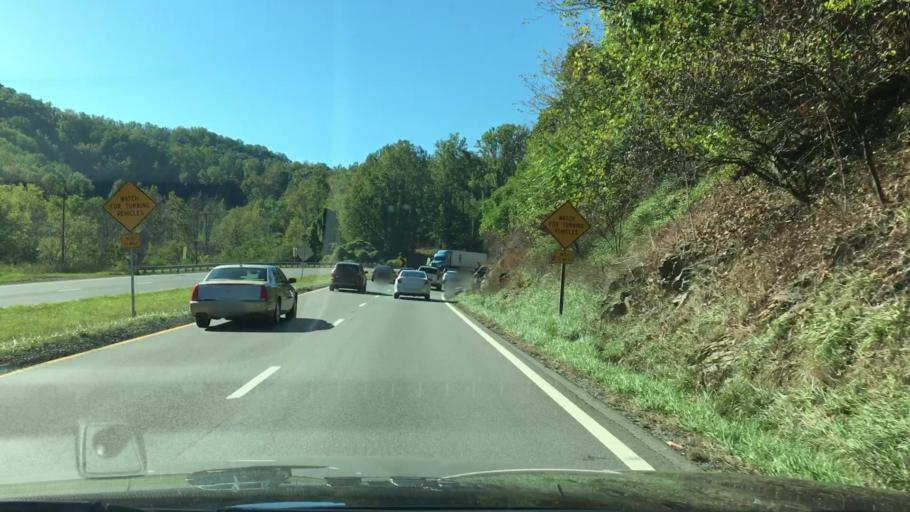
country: US
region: Virginia
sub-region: Roanoke County
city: Narrows
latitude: 37.1523
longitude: -79.9573
